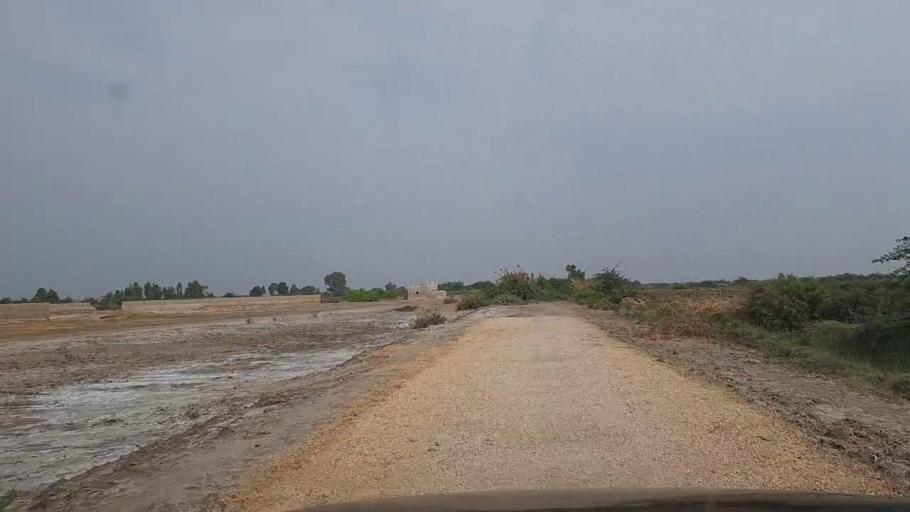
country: PK
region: Sindh
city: Thatta
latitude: 24.7517
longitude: 67.8271
